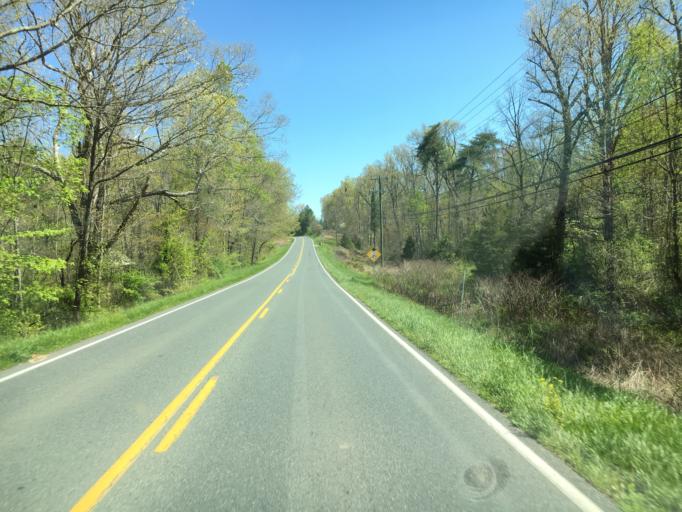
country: US
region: Virginia
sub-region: Augusta County
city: Crimora
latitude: 38.1433
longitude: -78.8426
